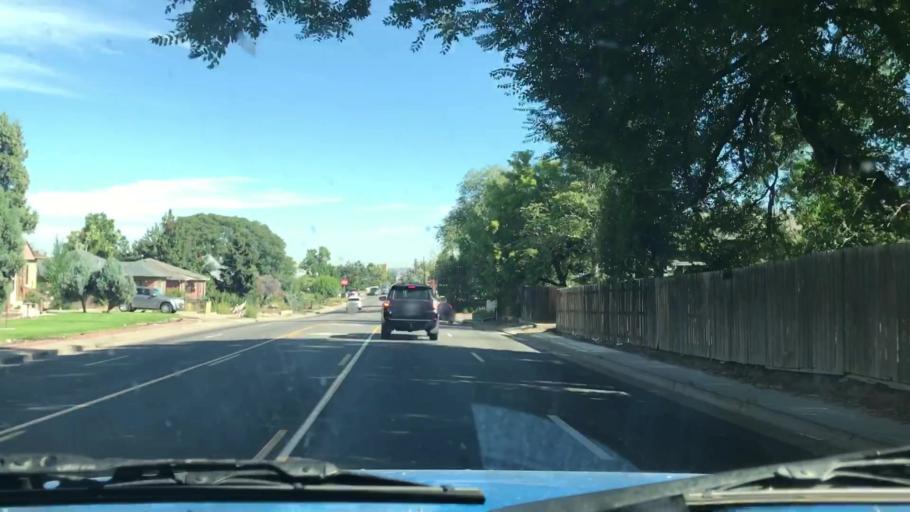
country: US
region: Colorado
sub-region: Jefferson County
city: Edgewater
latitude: 39.7667
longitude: -105.0532
